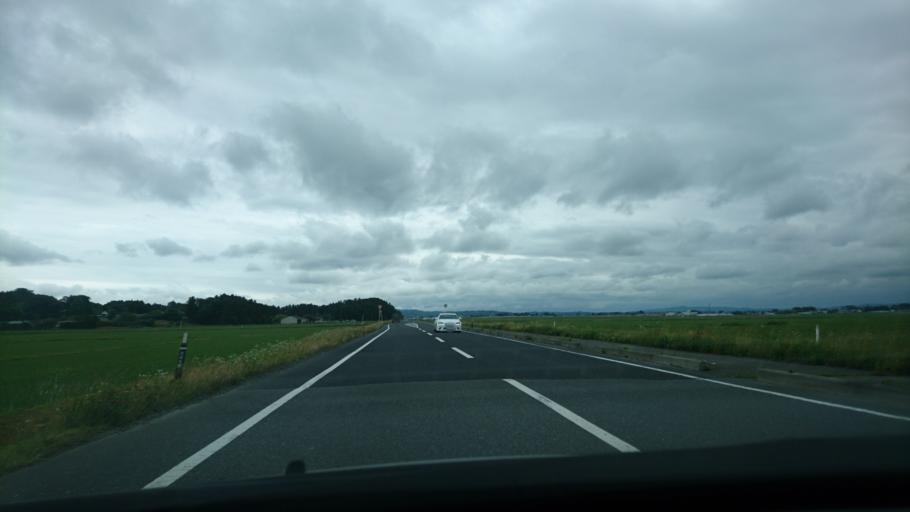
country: JP
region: Miyagi
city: Wakuya
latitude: 38.7015
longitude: 141.2602
